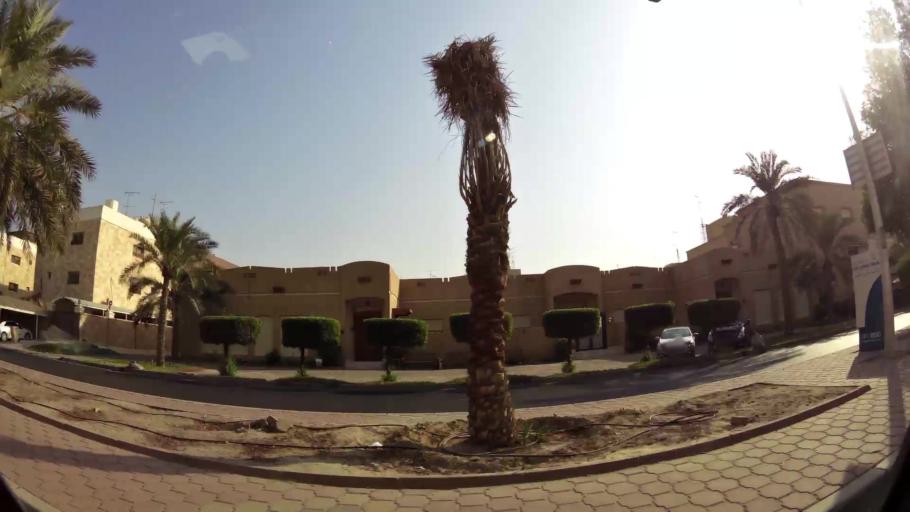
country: KW
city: Bayan
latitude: 29.3125
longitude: 48.0407
